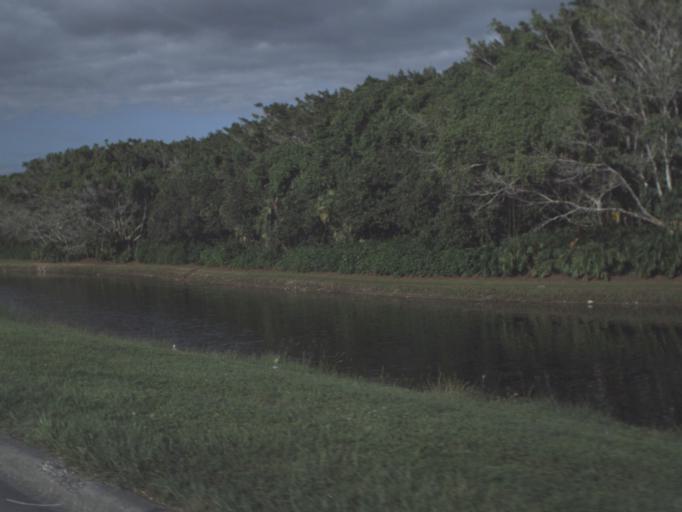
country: US
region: Florida
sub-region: Collier County
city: Naples
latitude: 26.1838
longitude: -81.7673
